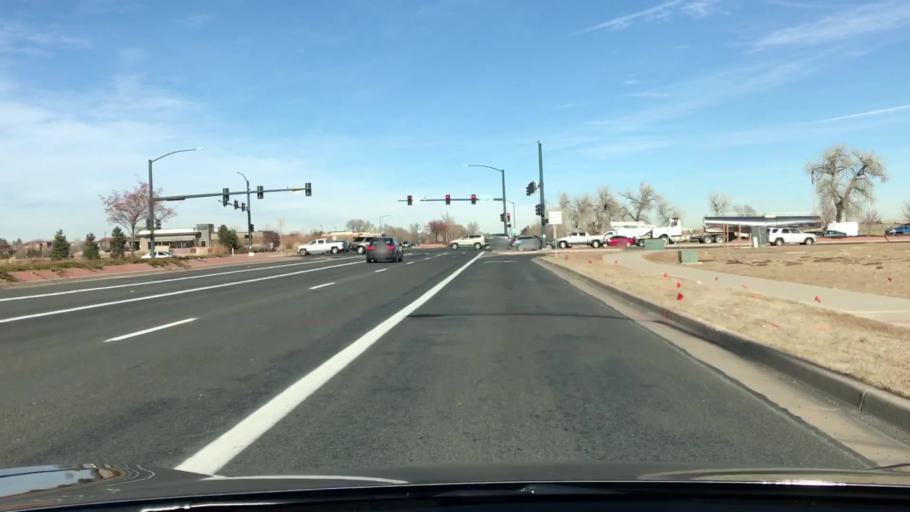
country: US
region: Colorado
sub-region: Adams County
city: Northglenn
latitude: 39.9423
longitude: -104.9967
